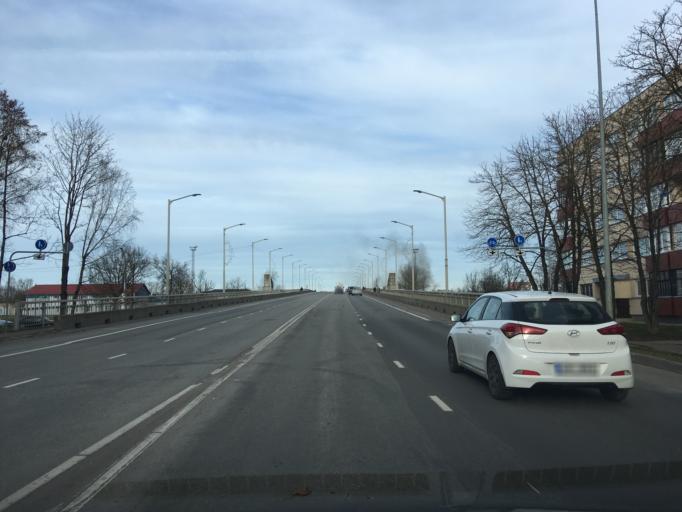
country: EE
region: Ida-Virumaa
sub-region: Narva linn
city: Narva
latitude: 59.3697
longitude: 28.1852
